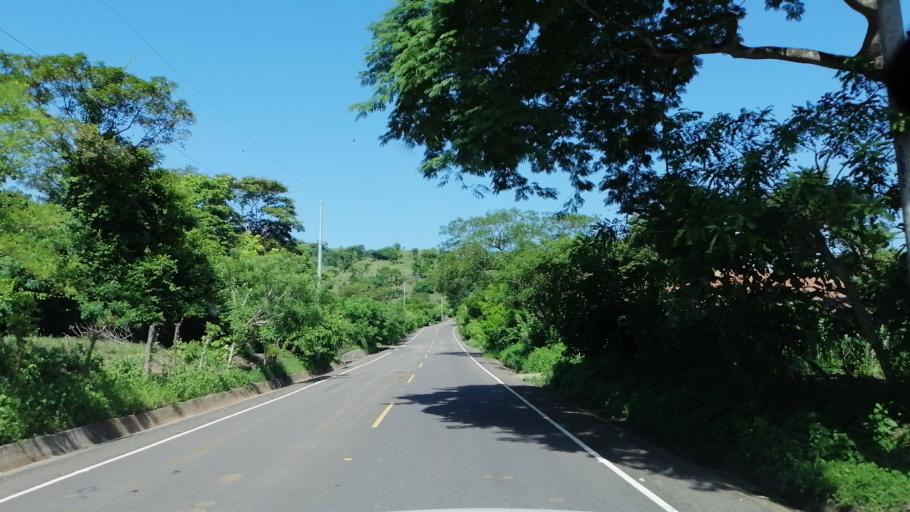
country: HN
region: Lempira
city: La Virtud
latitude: 13.9862
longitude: -88.7507
